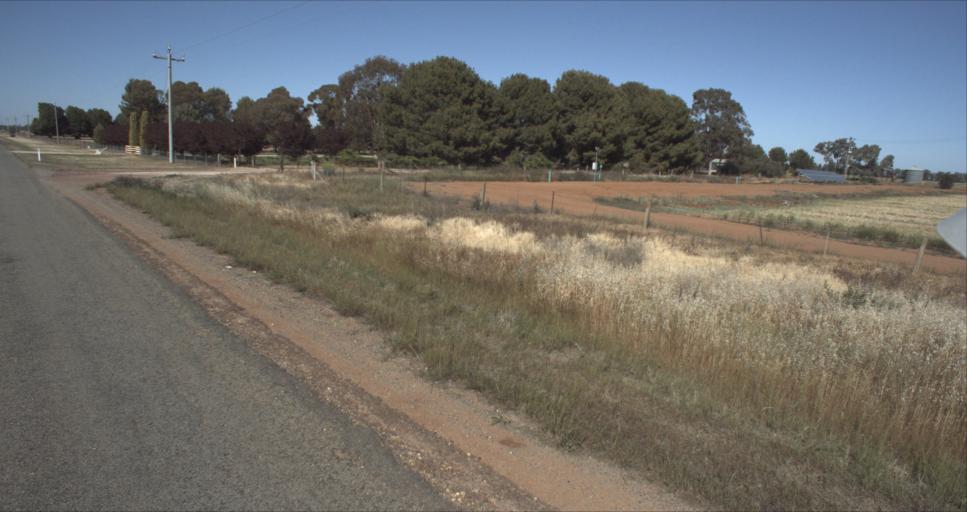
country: AU
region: New South Wales
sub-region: Leeton
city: Leeton
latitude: -34.5838
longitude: 146.2611
